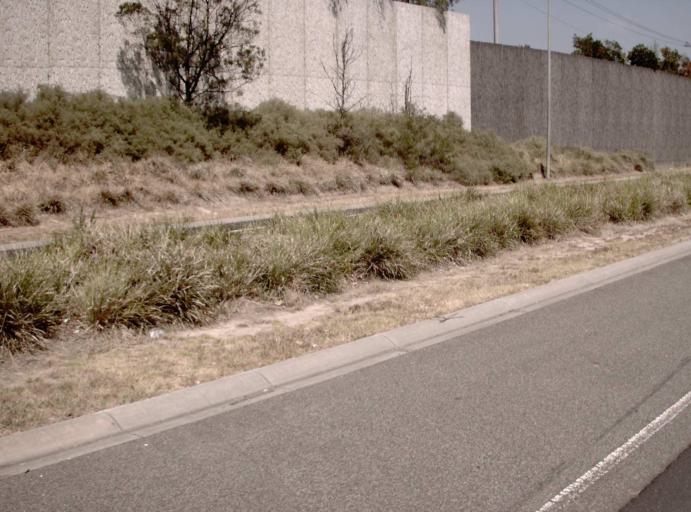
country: AU
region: Victoria
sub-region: Whitehorse
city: Box Hill North
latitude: -37.7973
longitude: 145.1307
